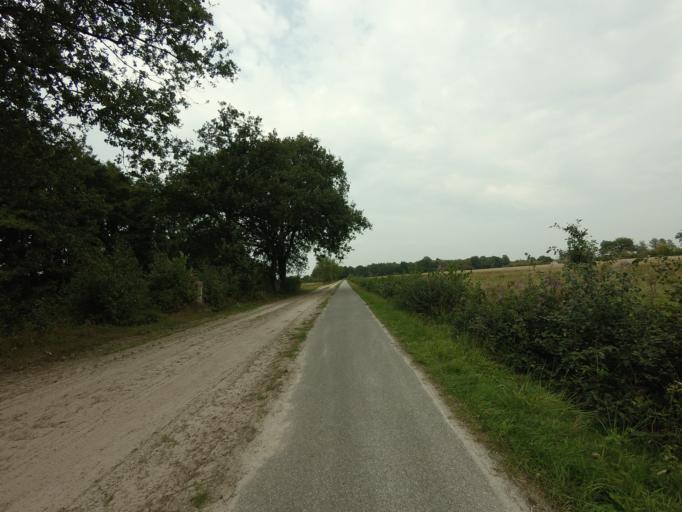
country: NL
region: Drenthe
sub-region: Gemeente Tynaarlo
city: Tynaarlo
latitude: 53.0170
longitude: 6.6328
